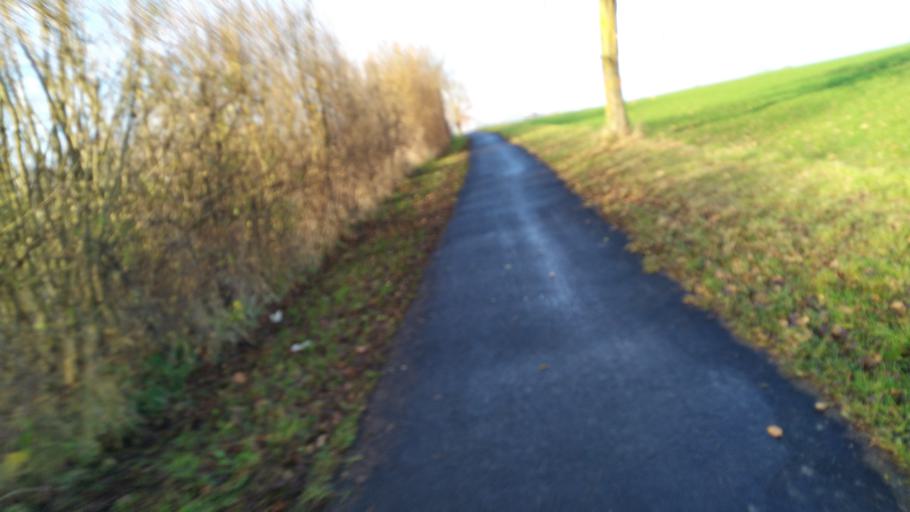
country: DE
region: Schleswig-Holstein
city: Travemuende
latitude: 53.9661
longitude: 10.8306
